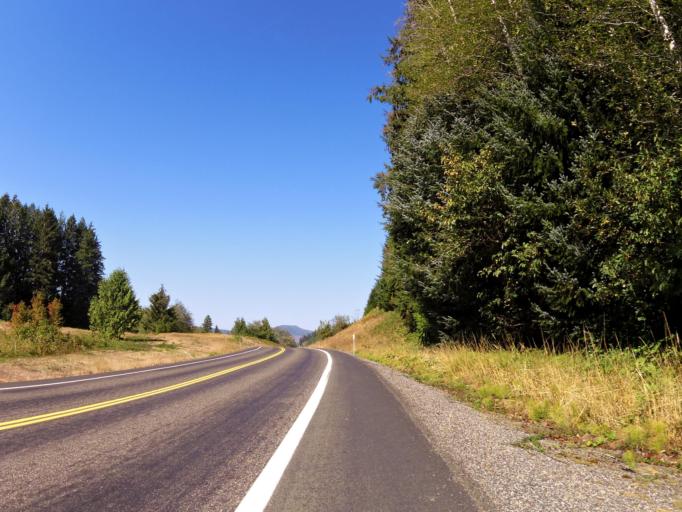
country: US
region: Oregon
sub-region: Tillamook County
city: Tillamook
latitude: 45.3219
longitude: -123.8436
